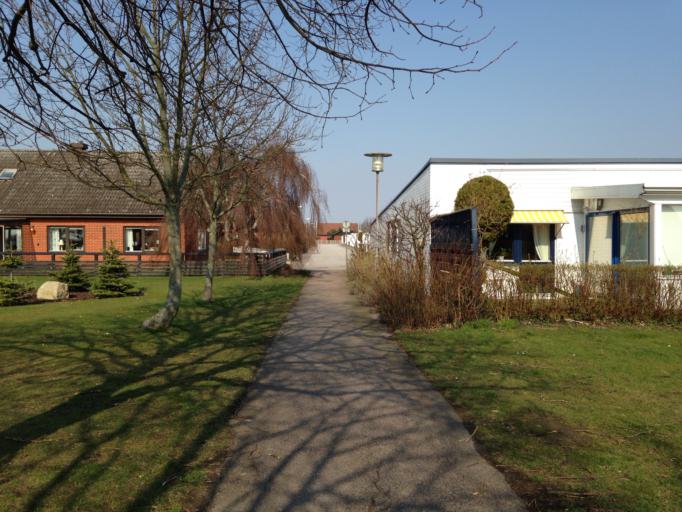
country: SE
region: Skane
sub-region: Staffanstorps Kommun
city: Hjaerup
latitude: 55.6704
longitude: 13.1372
